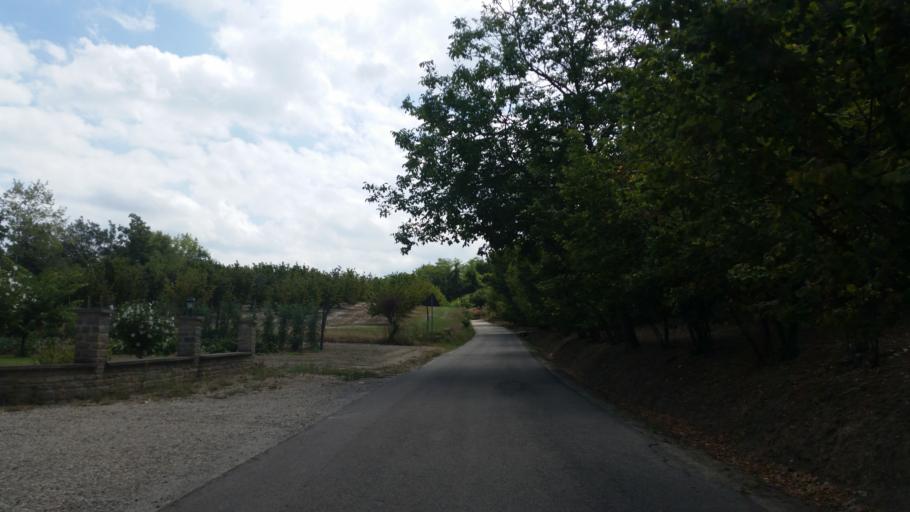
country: IT
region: Piedmont
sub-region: Provincia di Asti
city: Cessole
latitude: 44.6491
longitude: 8.2527
